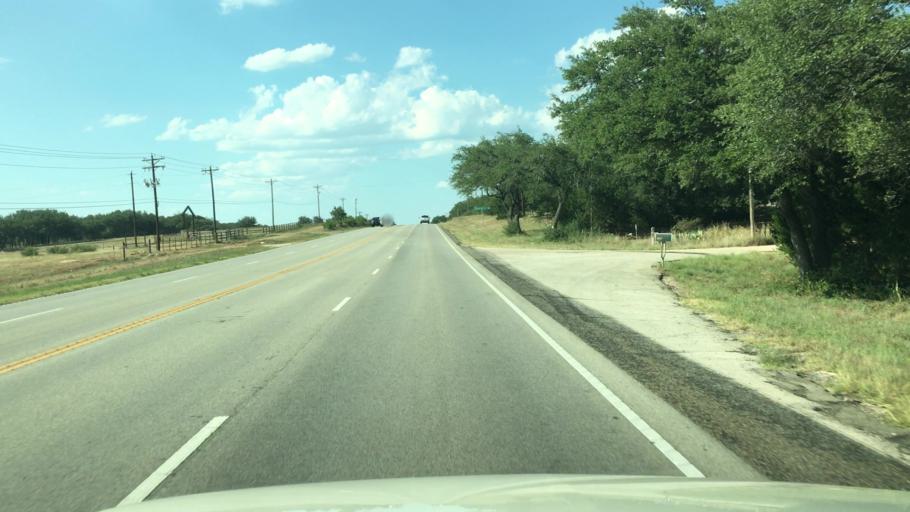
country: US
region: Texas
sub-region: Blanco County
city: Johnson City
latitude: 30.3210
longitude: -98.3891
